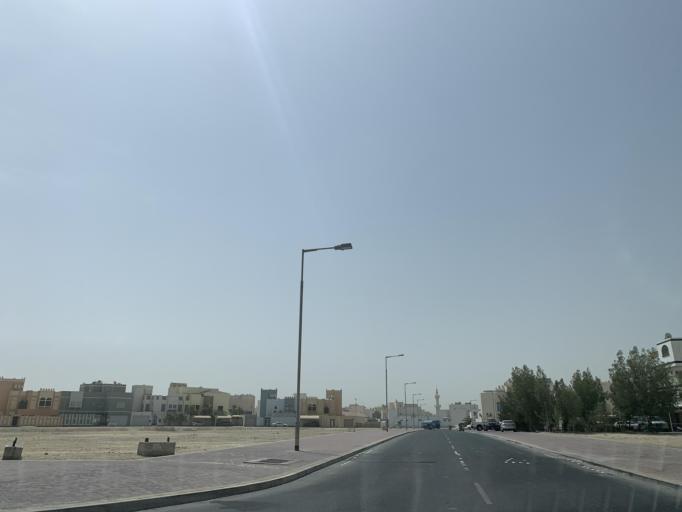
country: BH
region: Northern
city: Madinat `Isa
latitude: 26.1696
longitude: 50.5196
